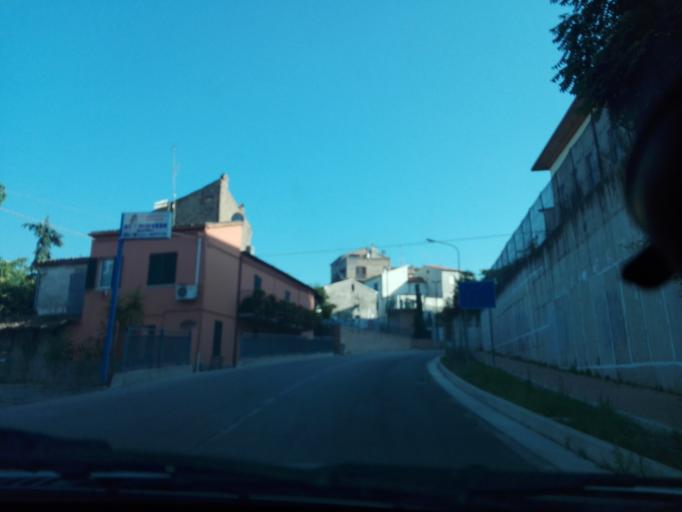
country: IT
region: Abruzzo
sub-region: Provincia di Pescara
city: Cappelle sul Tavo
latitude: 42.4660
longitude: 14.1039
